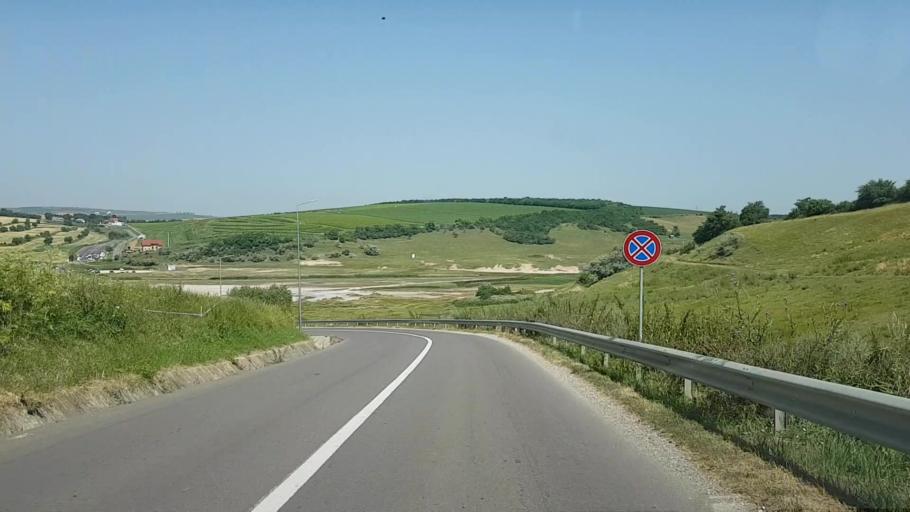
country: RO
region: Cluj
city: Turda
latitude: 46.5866
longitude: 23.7952
